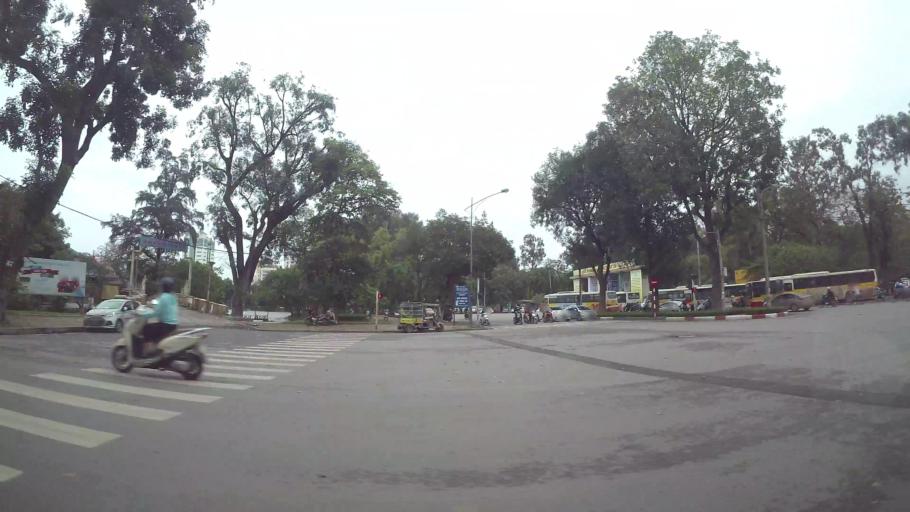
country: VN
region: Ha Noi
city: Hai BaTrung
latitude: 21.0175
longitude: 105.8436
